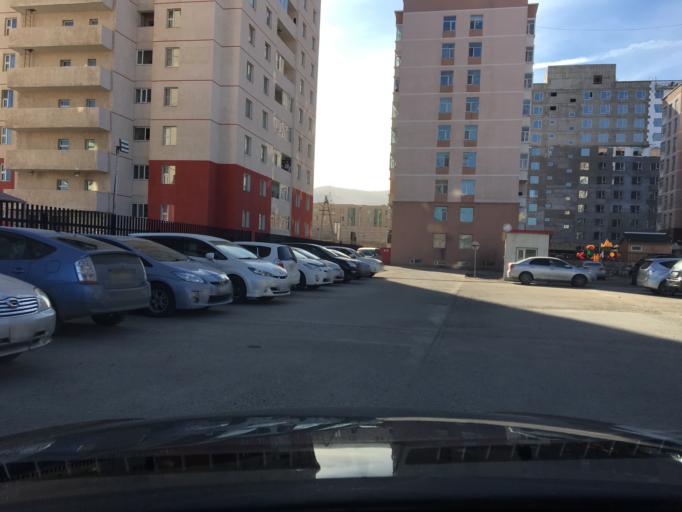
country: MN
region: Ulaanbaatar
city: Ulaanbaatar
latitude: 47.8924
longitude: 106.8948
